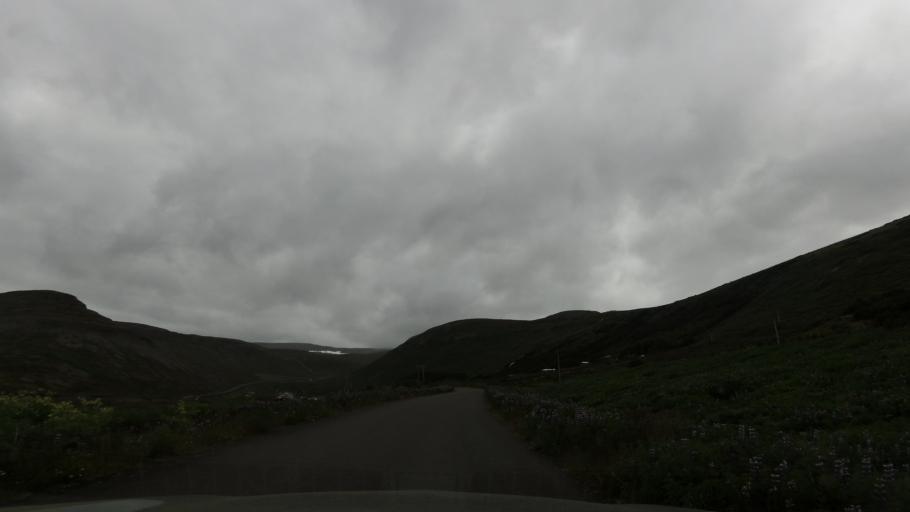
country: IS
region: Westfjords
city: Isafjoerdur
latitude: 66.0618
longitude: -23.1858
